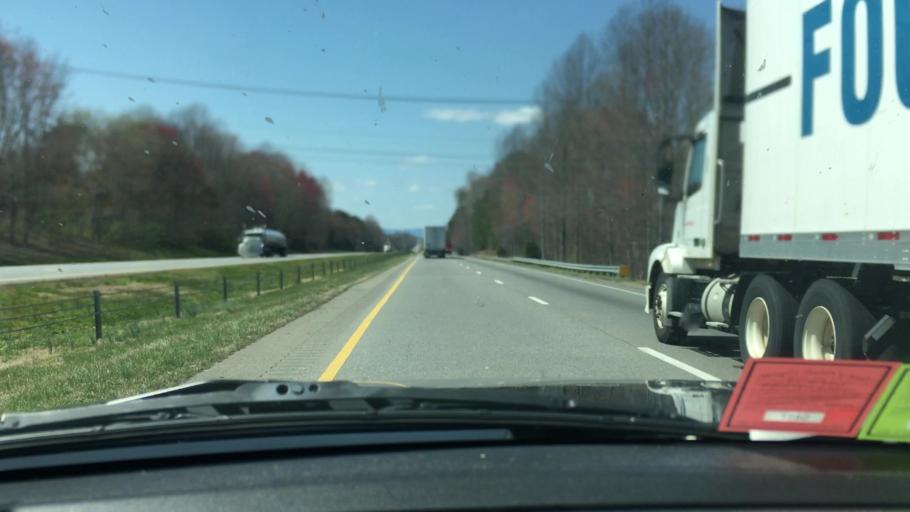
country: US
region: North Carolina
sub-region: Surry County
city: Pilot Mountain
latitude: 36.4188
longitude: -80.5118
